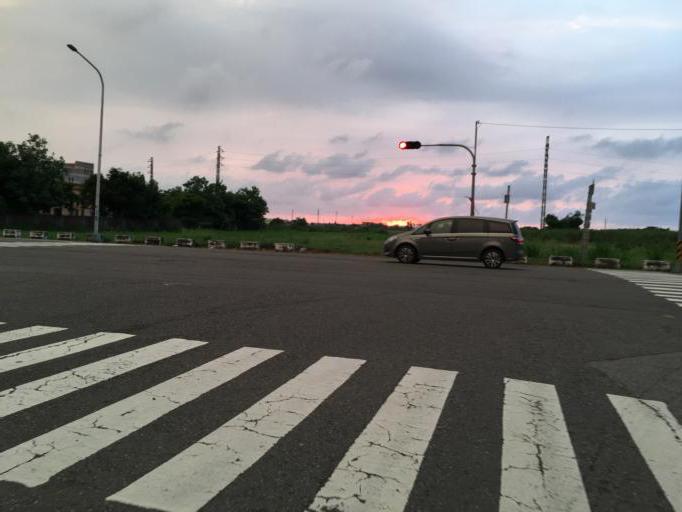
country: TW
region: Taiwan
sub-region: Chiayi
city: Taibao
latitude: 23.4587
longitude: 120.2852
